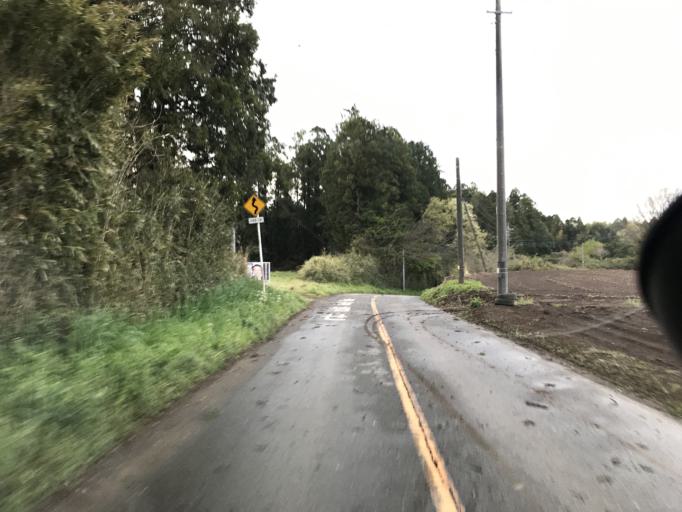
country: JP
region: Chiba
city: Sawara
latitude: 35.7767
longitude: 140.4509
